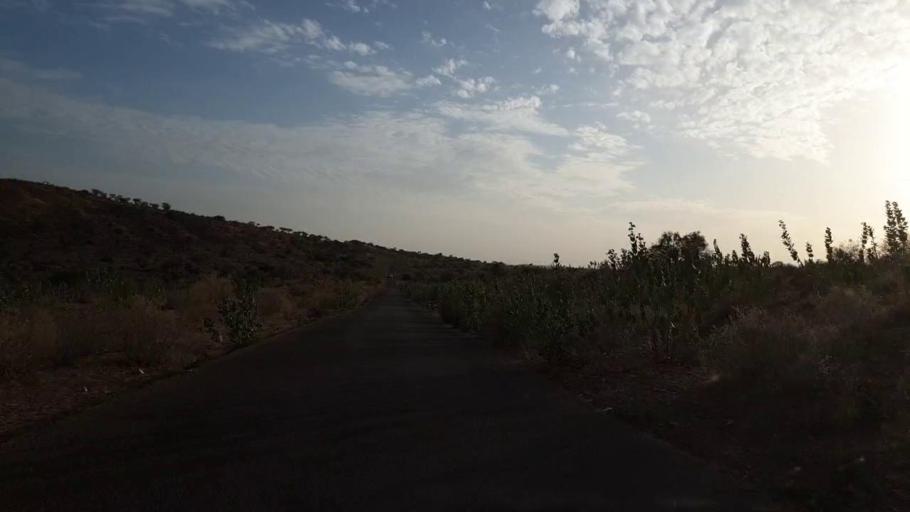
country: PK
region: Sindh
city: Umarkot
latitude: 25.1209
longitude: 70.0012
